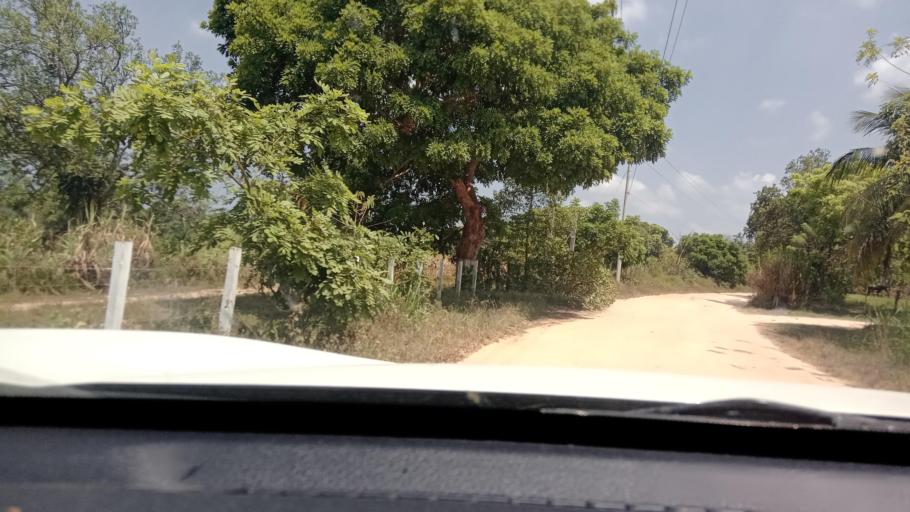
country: MX
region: Veracruz
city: Las Choapas
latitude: 17.9372
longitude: -94.1180
